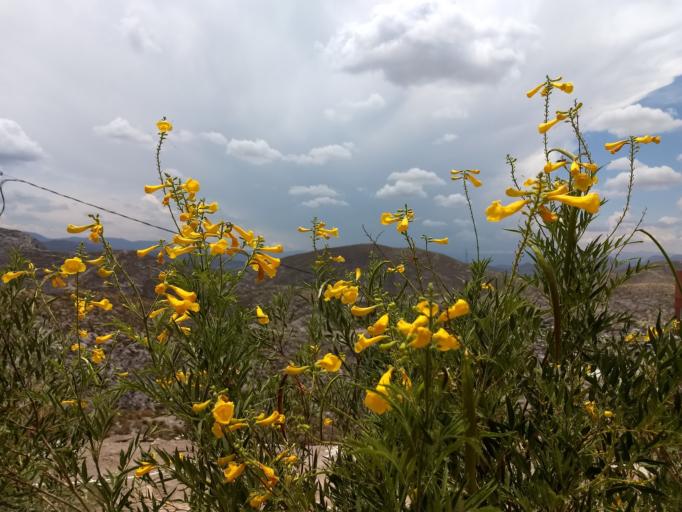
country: MX
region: Durango
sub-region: Lerdo
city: El Huarache (El Guarache)
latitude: 25.5260
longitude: -103.4566
